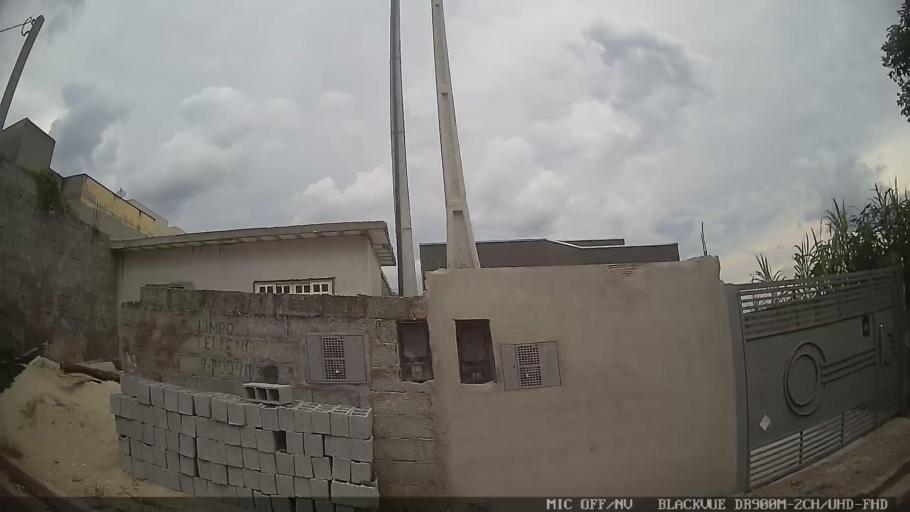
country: BR
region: Sao Paulo
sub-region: Atibaia
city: Atibaia
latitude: -23.1313
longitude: -46.5923
